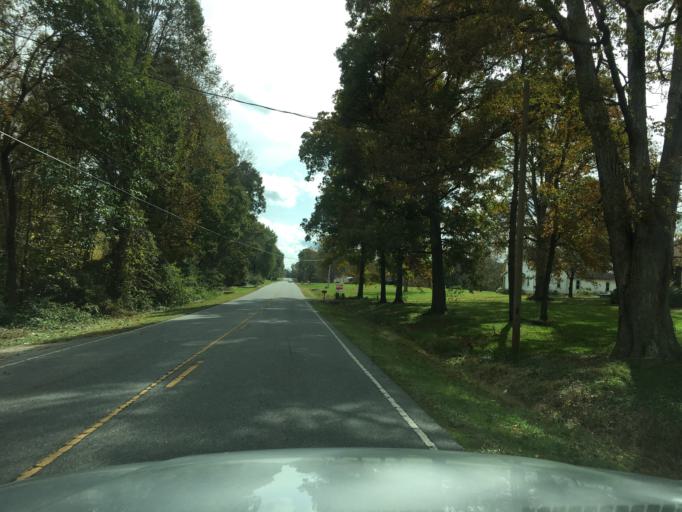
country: US
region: North Carolina
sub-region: Catawba County
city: Newton
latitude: 35.6754
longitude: -81.2737
